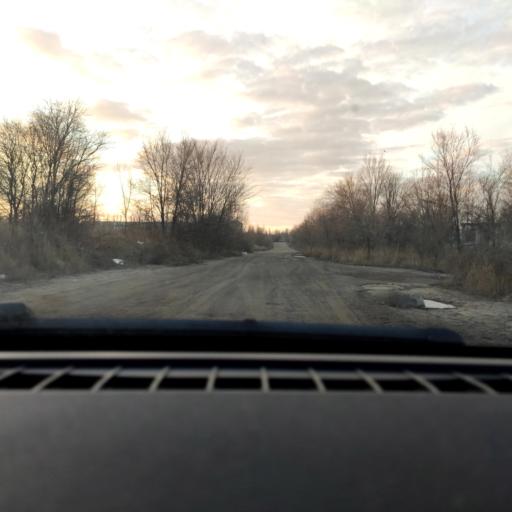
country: RU
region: Voronezj
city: Maslovka
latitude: 51.6095
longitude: 39.2666
